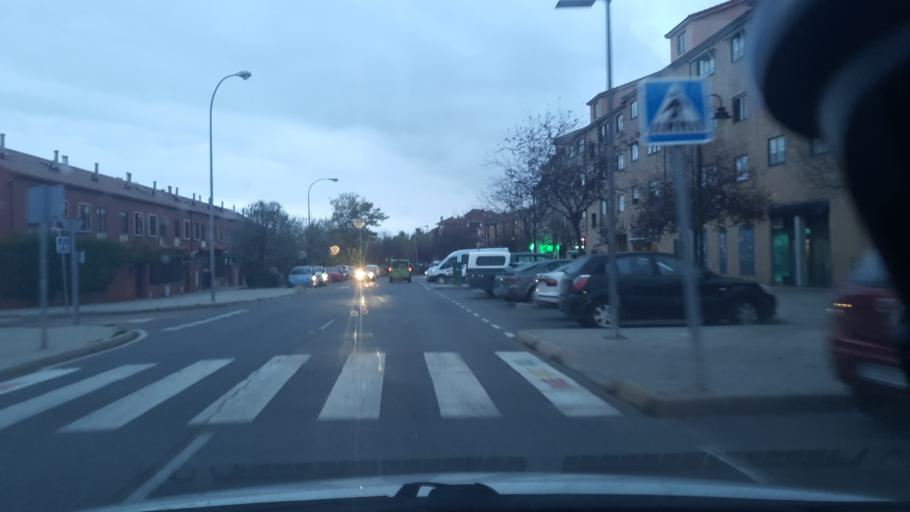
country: ES
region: Castille and Leon
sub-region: Provincia de Segovia
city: Segovia
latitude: 40.9299
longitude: -4.1012
